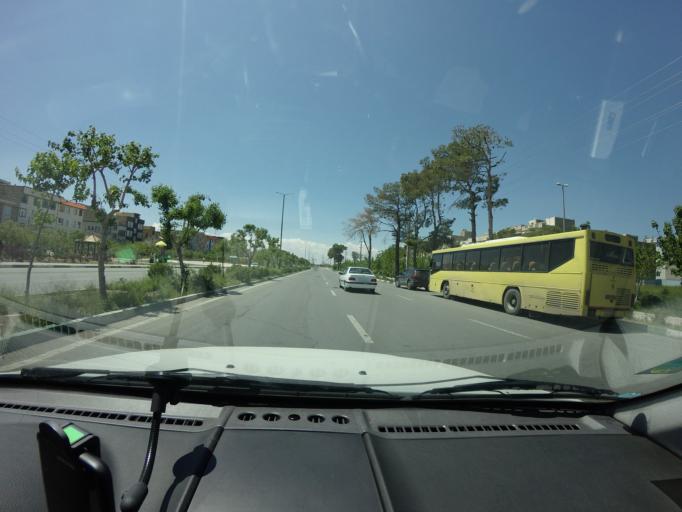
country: IR
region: Tehran
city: Eslamshahr
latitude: 35.5314
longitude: 51.2146
